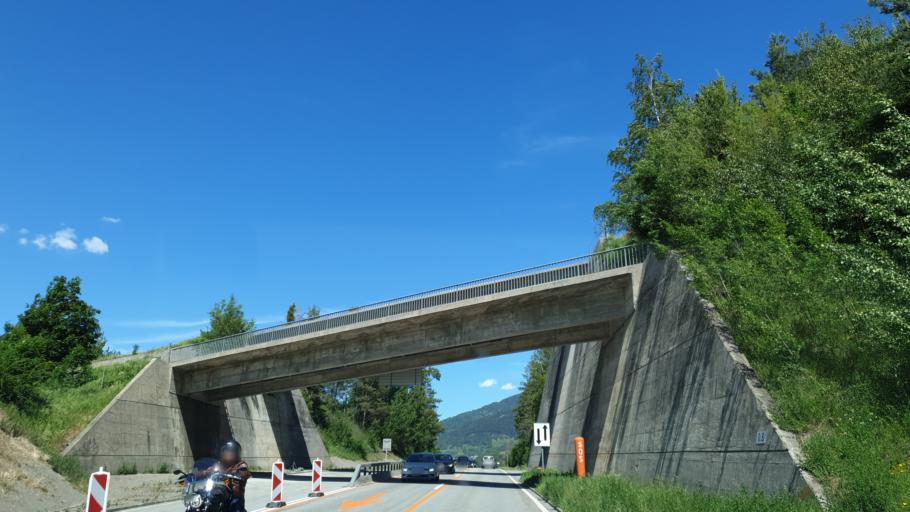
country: CH
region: Valais
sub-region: Brig District
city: Brig
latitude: 46.3055
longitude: 7.9710
